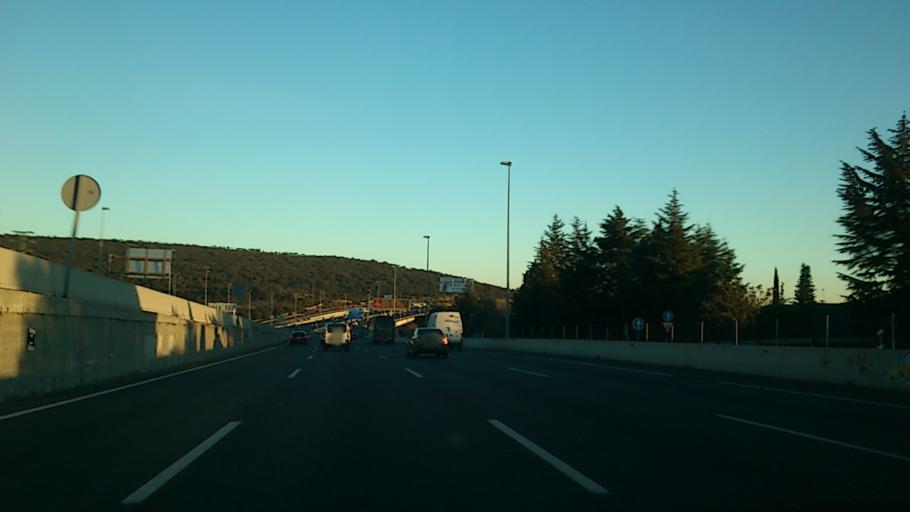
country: ES
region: Madrid
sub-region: Provincia de Madrid
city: Galapagar
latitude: 40.6058
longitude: -3.9705
